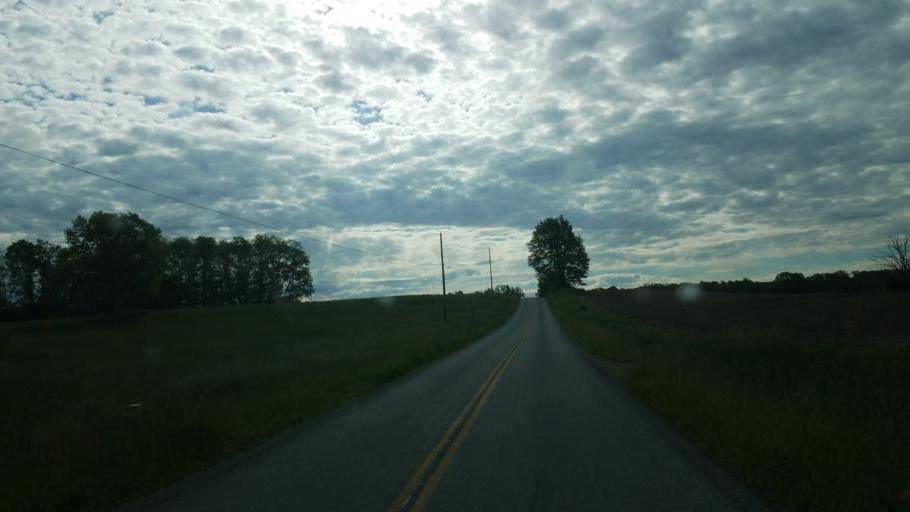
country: US
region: Ohio
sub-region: Medina County
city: Westfield Center
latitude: 40.9857
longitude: -81.9385
